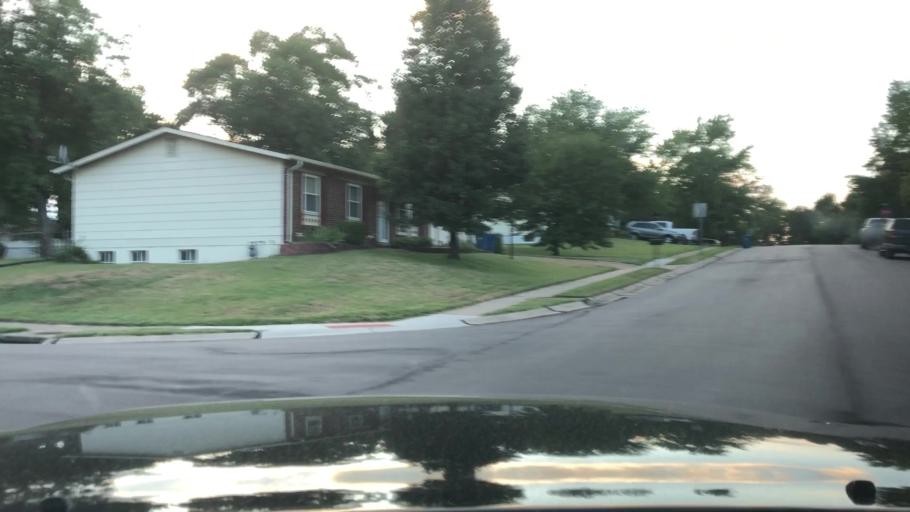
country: US
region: Missouri
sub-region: Saint Charles County
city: Saint Charles
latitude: 38.8121
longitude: -90.5068
